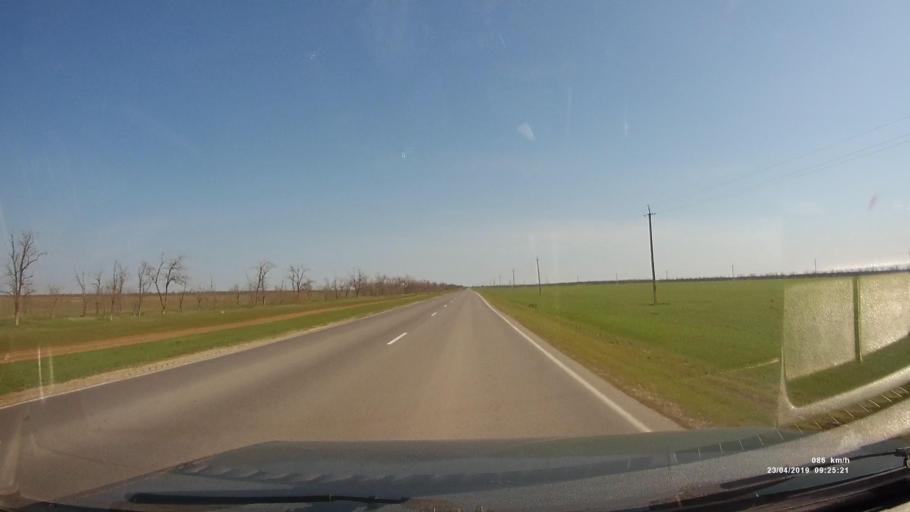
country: RU
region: Rostov
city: Proletarsk
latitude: 46.7147
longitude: 41.7623
